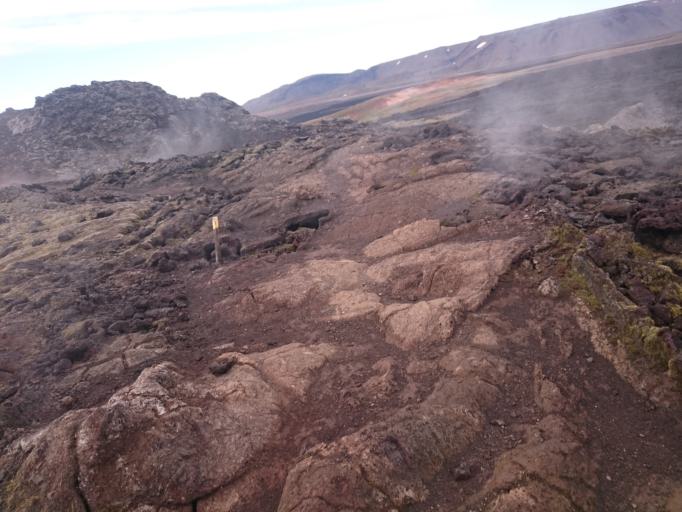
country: IS
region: Northeast
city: Laugar
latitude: 65.7225
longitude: -16.7935
